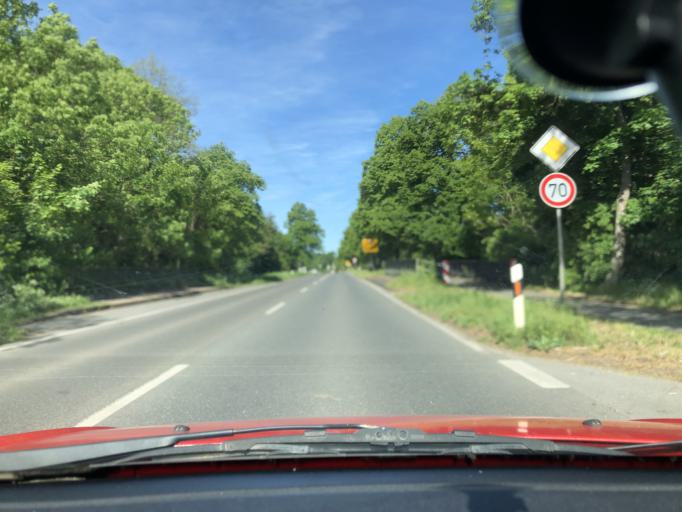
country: DE
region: North Rhine-Westphalia
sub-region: Regierungsbezirk Dusseldorf
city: Moers
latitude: 51.4933
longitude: 6.6138
